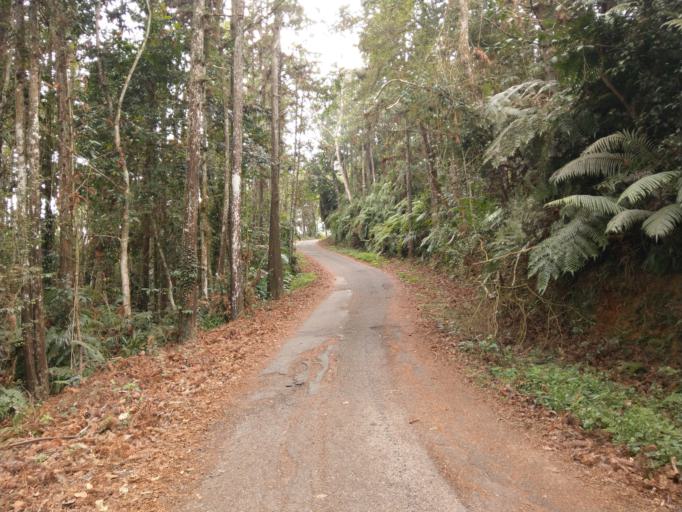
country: TW
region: Taiwan
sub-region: Nantou
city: Puli
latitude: 23.8796
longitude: 120.9121
